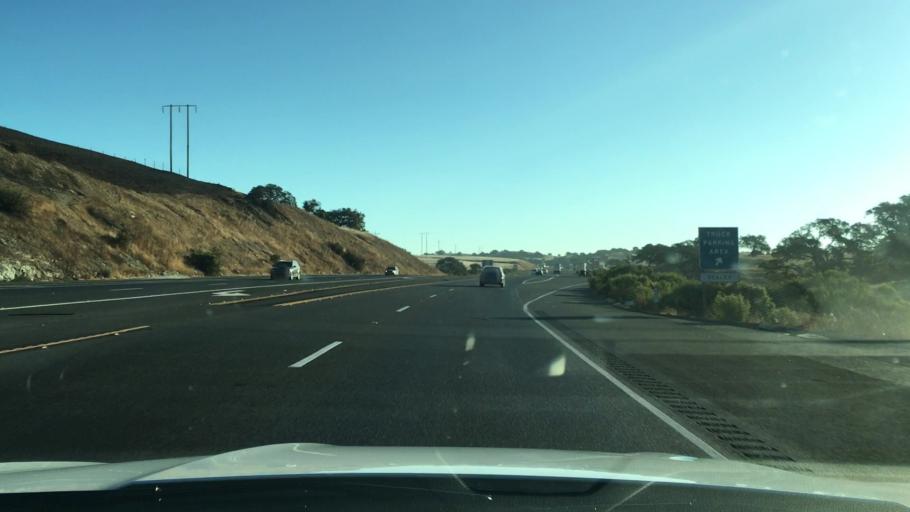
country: US
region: California
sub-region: San Benito County
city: Hollister
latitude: 37.0647
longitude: -121.2261
